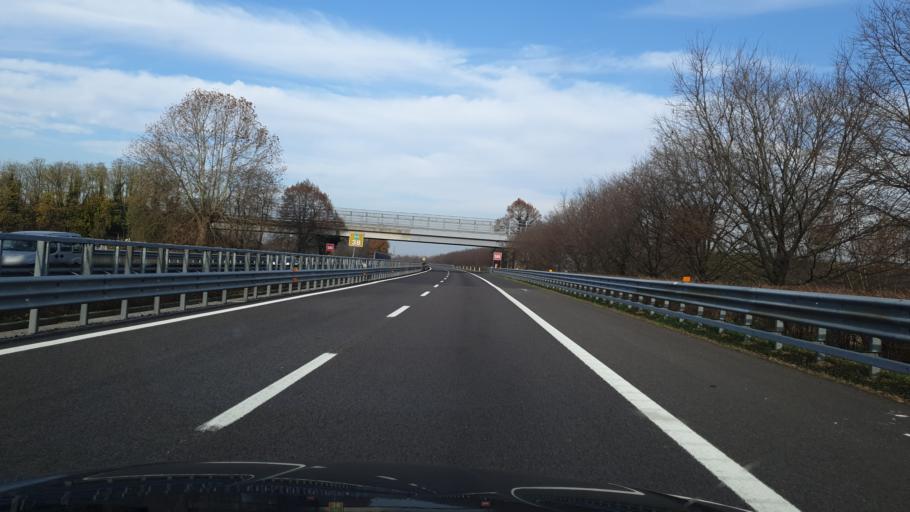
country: IT
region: Veneto
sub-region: Provincia di Vicenza
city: Vigardolo
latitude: 45.6099
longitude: 11.6006
